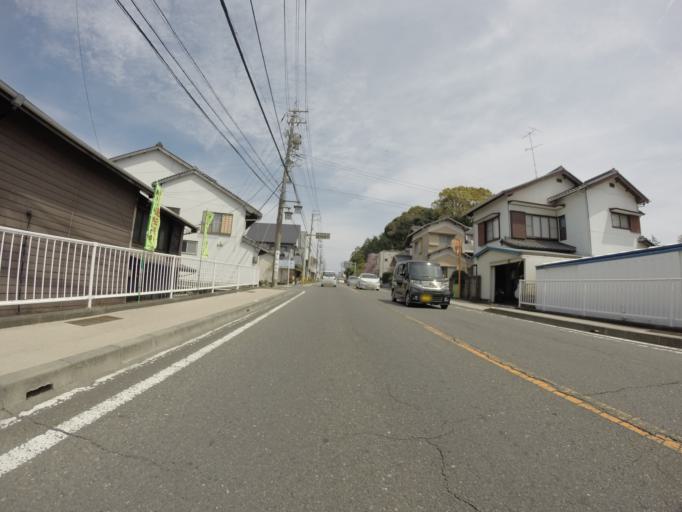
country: JP
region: Shizuoka
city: Fujinomiya
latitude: 35.1088
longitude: 138.5656
